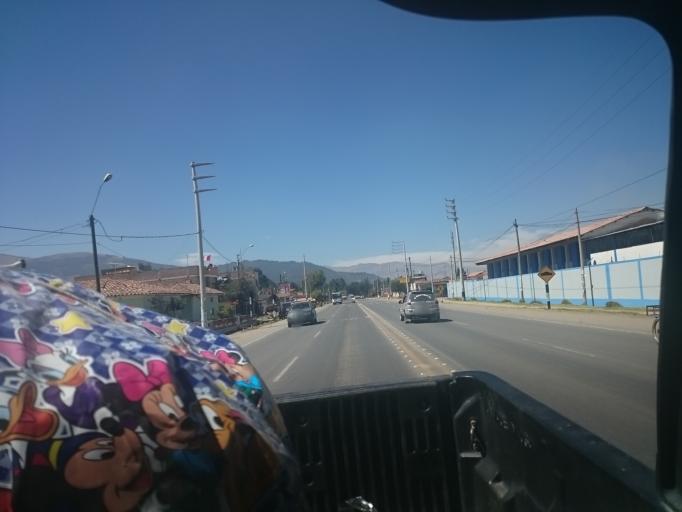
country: PE
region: Junin
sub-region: Provincia de Huancayo
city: San Jeronimo
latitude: -11.9531
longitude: -75.2816
